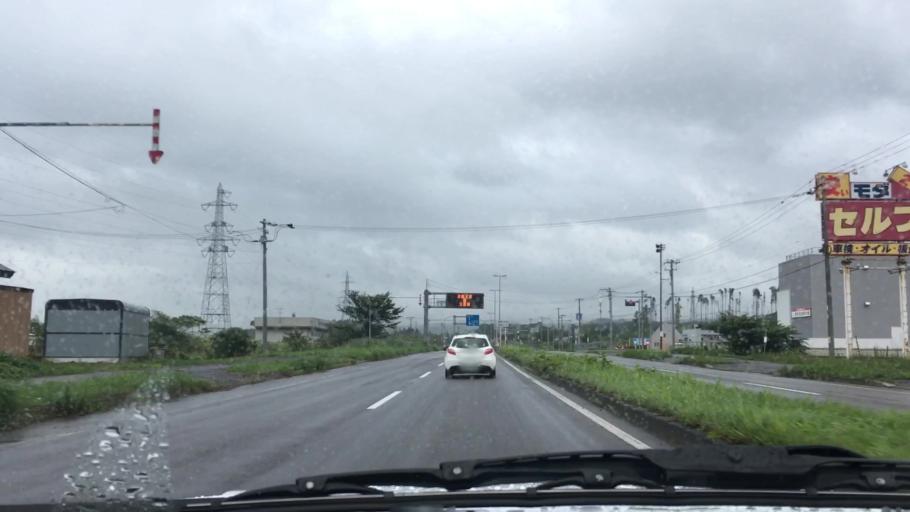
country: JP
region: Hokkaido
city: Nanae
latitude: 42.2478
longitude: 140.2881
